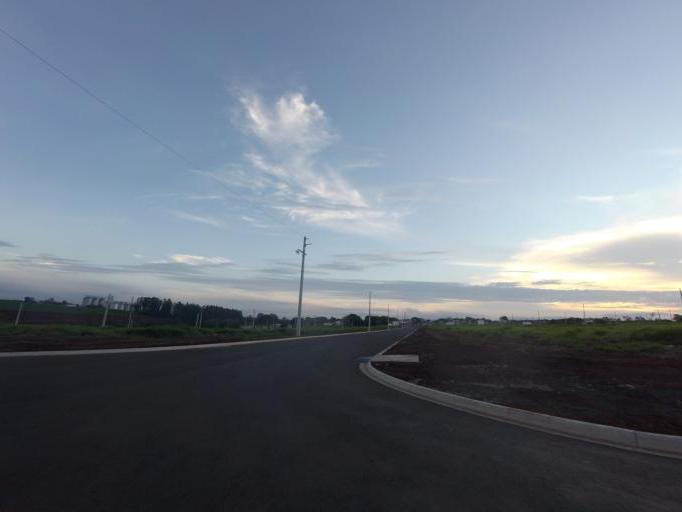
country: BR
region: Sao Paulo
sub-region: Piracicaba
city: Piracicaba
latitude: -22.7637
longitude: -47.5835
